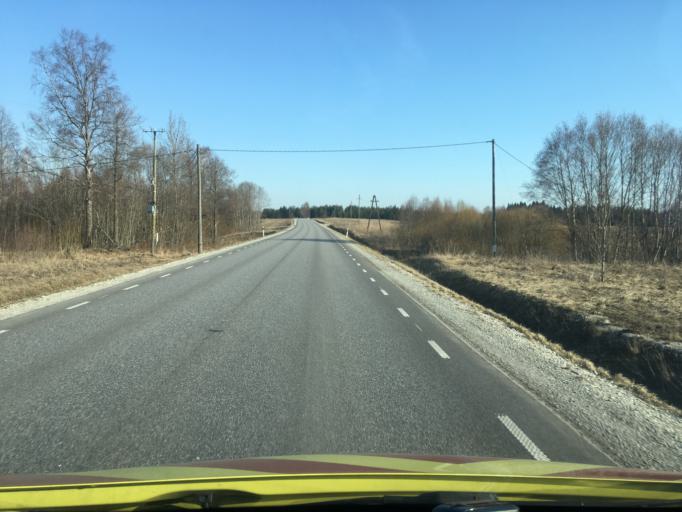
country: EE
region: Raplamaa
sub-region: Rapla vald
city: Rapla
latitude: 59.0017
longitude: 24.8426
